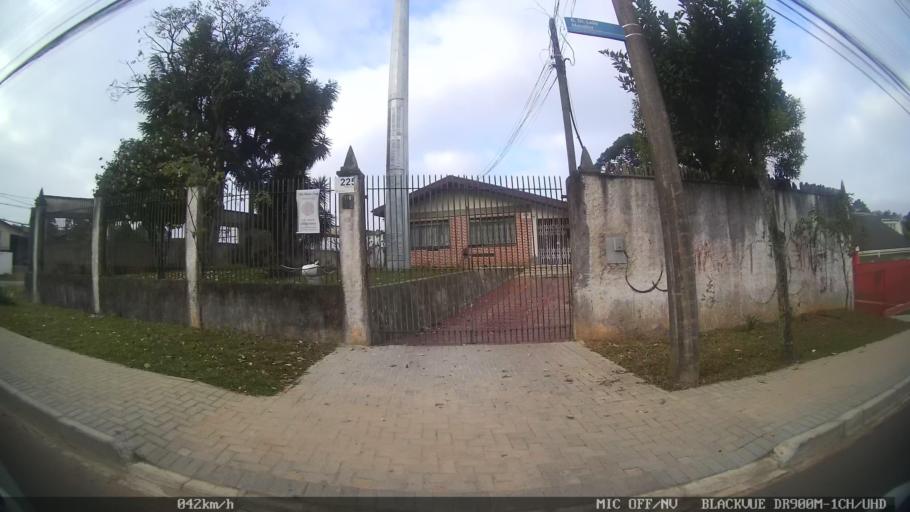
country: BR
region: Parana
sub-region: Curitiba
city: Curitiba
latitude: -25.3984
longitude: -49.3196
